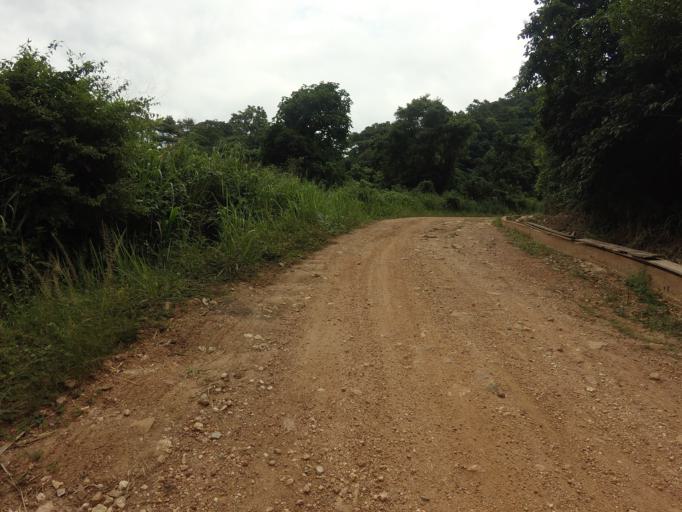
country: GH
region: Volta
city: Kpandu
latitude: 6.8735
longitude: 0.4282
